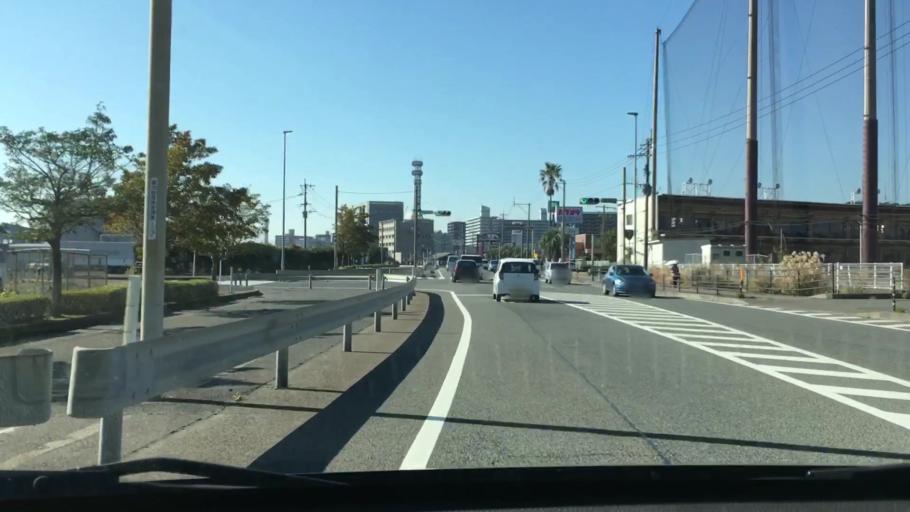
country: JP
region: Kagoshima
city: Kagoshima-shi
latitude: 31.6031
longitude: 130.5676
